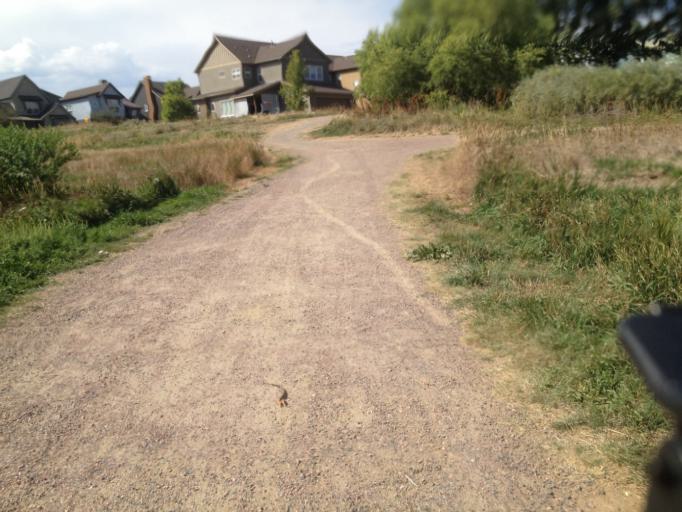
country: US
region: Colorado
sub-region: Boulder County
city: Louisville
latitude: 39.9924
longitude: -105.1228
